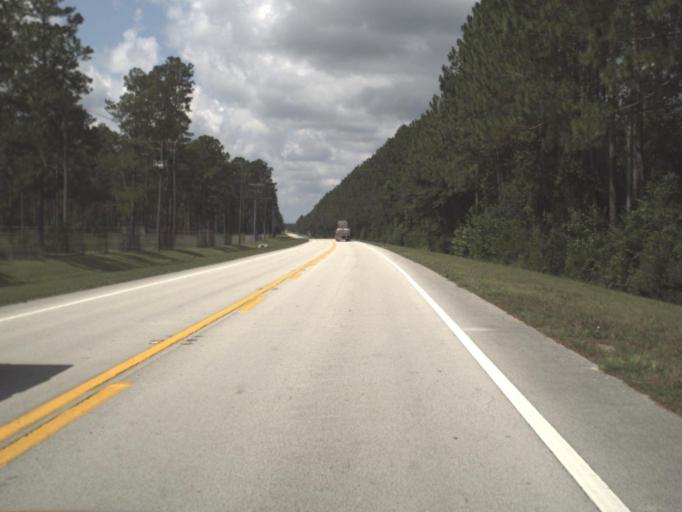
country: US
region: Florida
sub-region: Baker County
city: Macclenny
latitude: 30.2351
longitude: -82.1404
